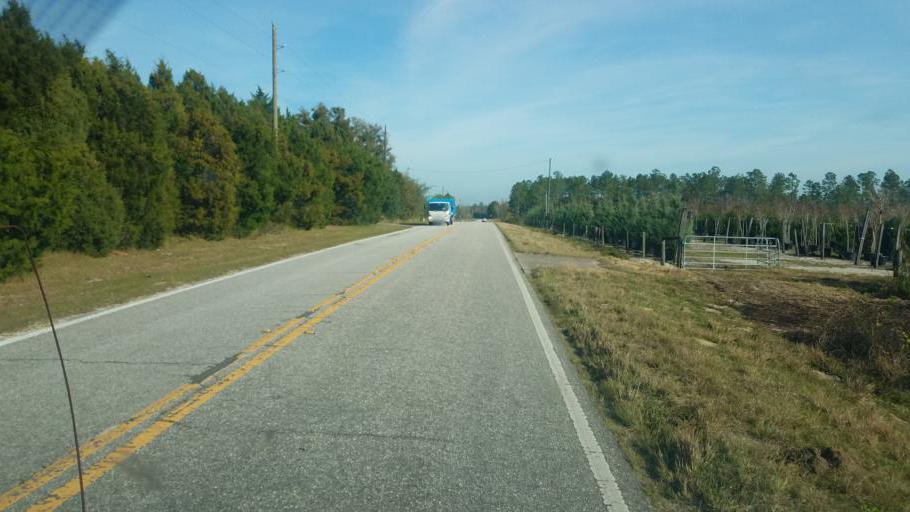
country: US
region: Florida
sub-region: Lake County
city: Clermont
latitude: 28.4507
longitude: -81.7964
